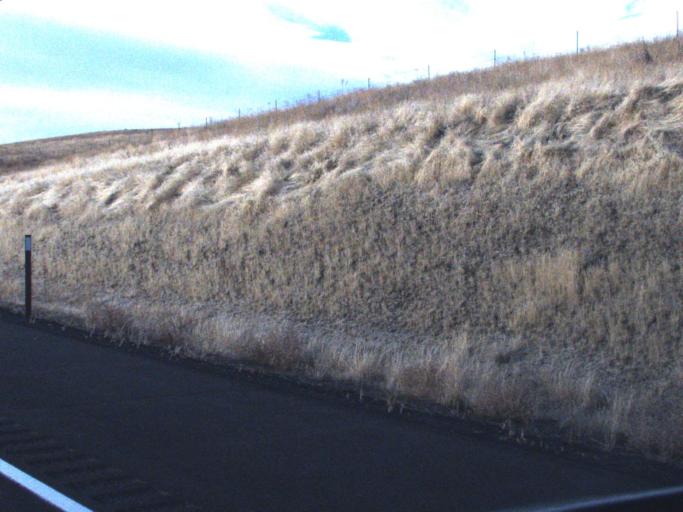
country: US
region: Washington
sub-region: Adams County
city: Ritzville
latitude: 46.8932
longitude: -118.6152
